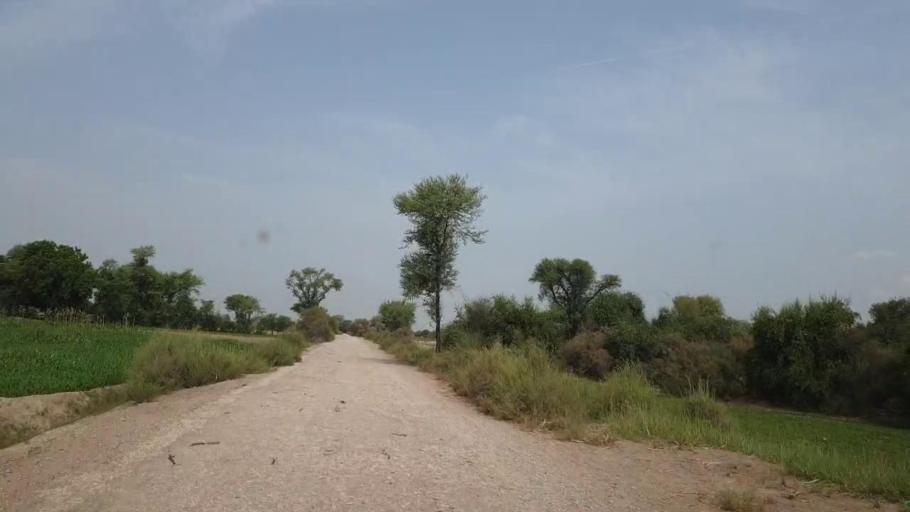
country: PK
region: Sindh
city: Sobhadero
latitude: 27.3924
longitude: 68.2660
